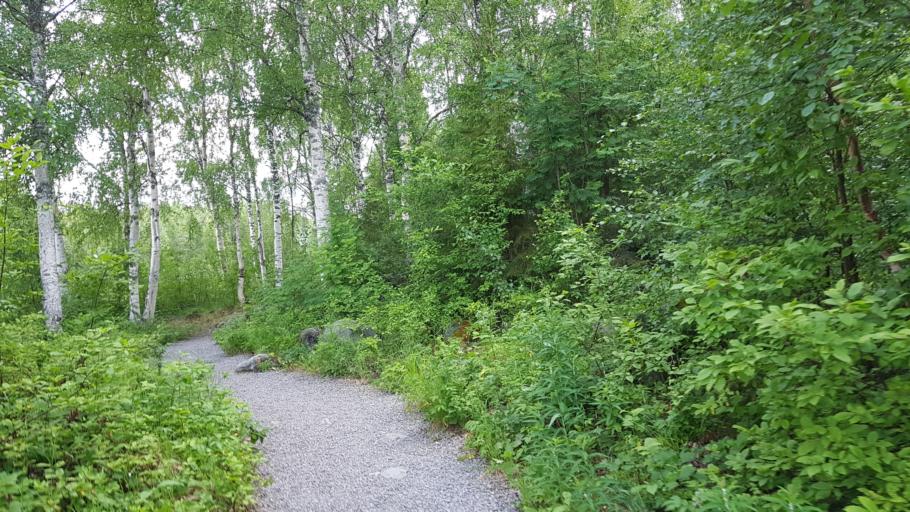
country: SE
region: Norrbotten
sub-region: Alvsbyns Kommun
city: AElvsbyn
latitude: 65.8547
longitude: 20.4152
